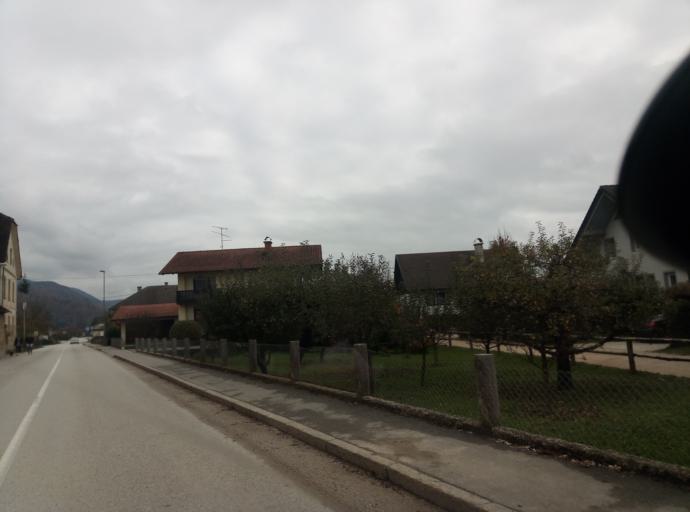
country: SI
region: Sencur
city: Sencur
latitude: 46.2656
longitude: 14.4506
